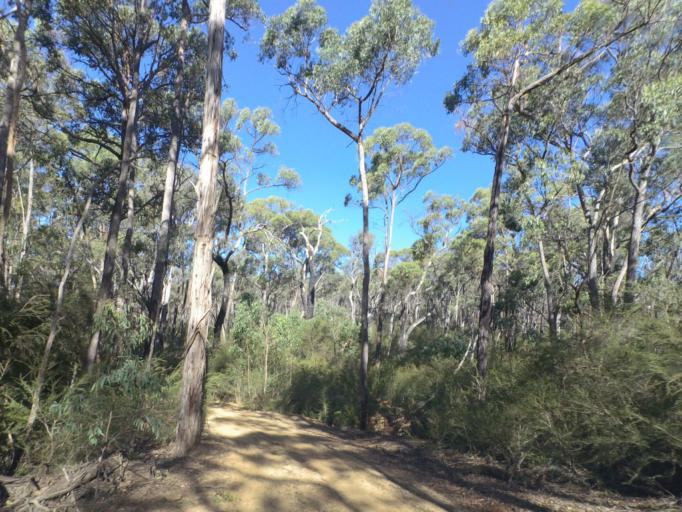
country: AU
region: Victoria
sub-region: Murrindindi
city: Kinglake West
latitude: -37.4634
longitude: 145.3715
